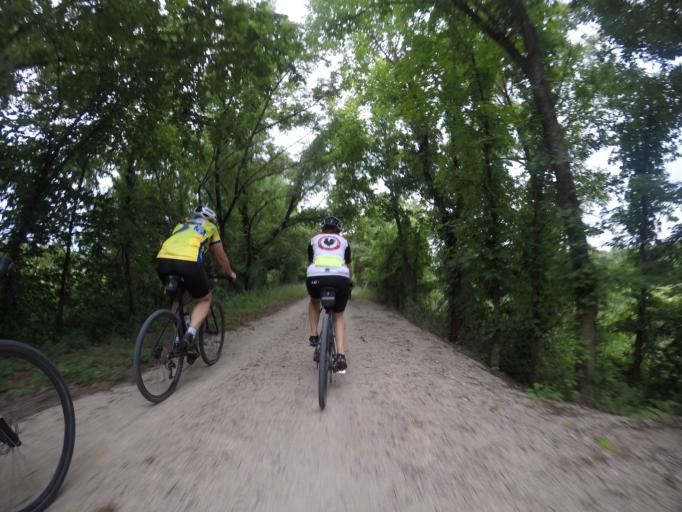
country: US
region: Kansas
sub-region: Anderson County
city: Garnett
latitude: 38.2522
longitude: -95.2527
